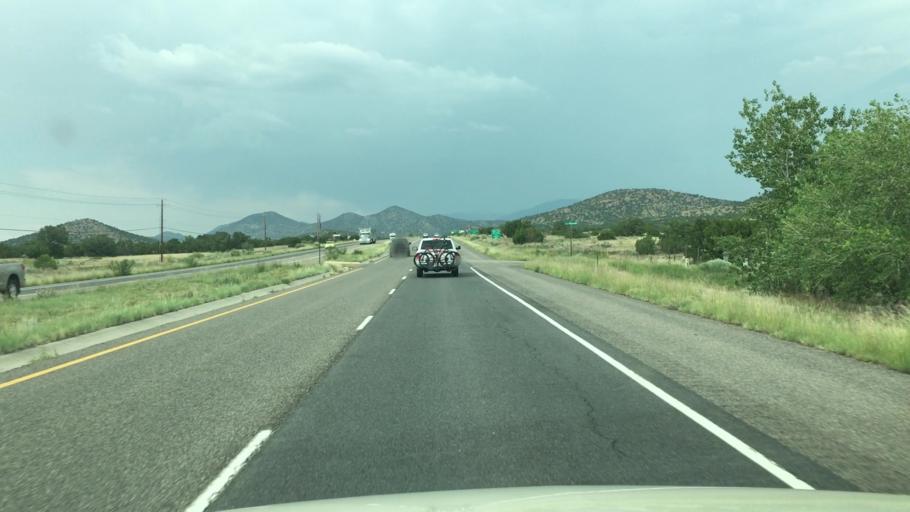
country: US
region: New Mexico
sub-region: Santa Fe County
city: Eldorado at Santa Fe
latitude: 35.5268
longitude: -105.8905
